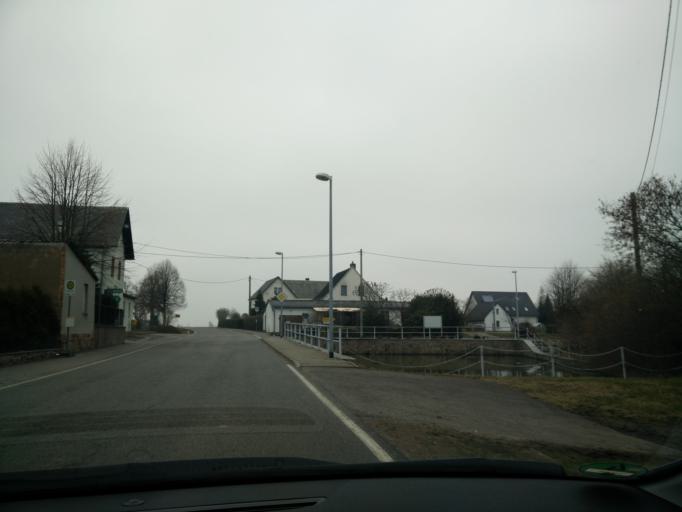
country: DE
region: Saxony
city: Narsdorf
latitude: 51.0115
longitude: 12.7387
